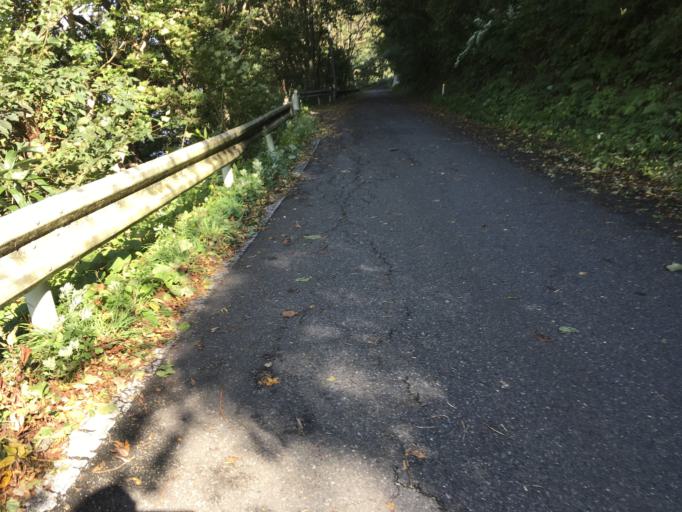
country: JP
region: Iwate
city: Ichinoseki
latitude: 38.8294
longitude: 141.2594
